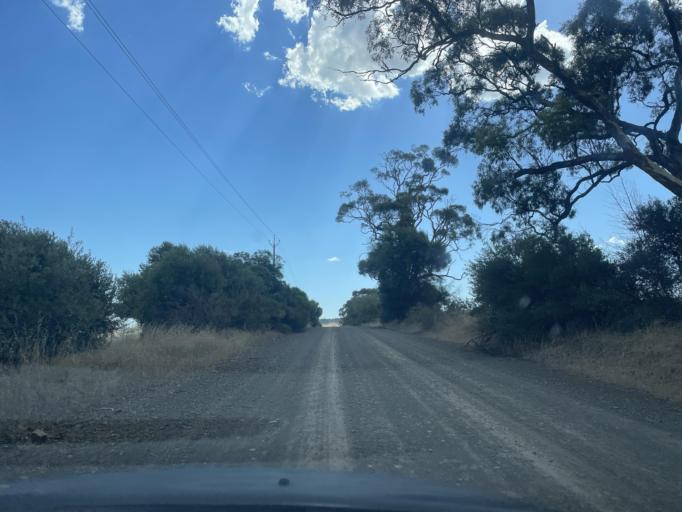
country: AU
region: South Australia
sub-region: Clare and Gilbert Valleys
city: Clare
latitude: -33.9096
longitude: 138.7325
